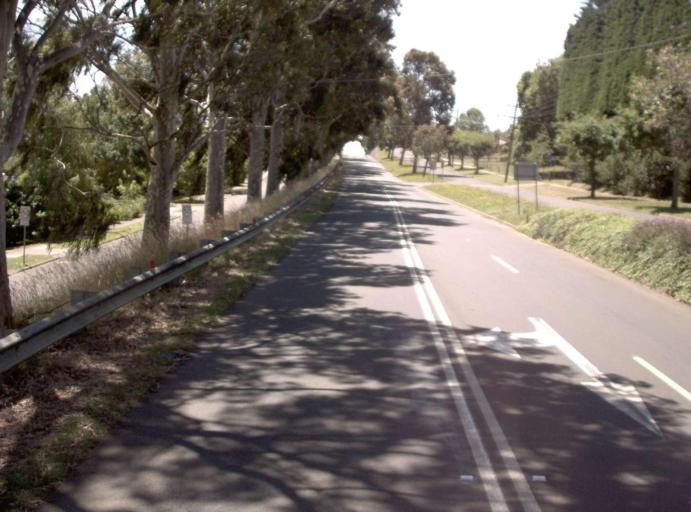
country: AU
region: Victoria
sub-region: Baw Baw
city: Warragul
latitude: -38.0132
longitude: 145.9552
